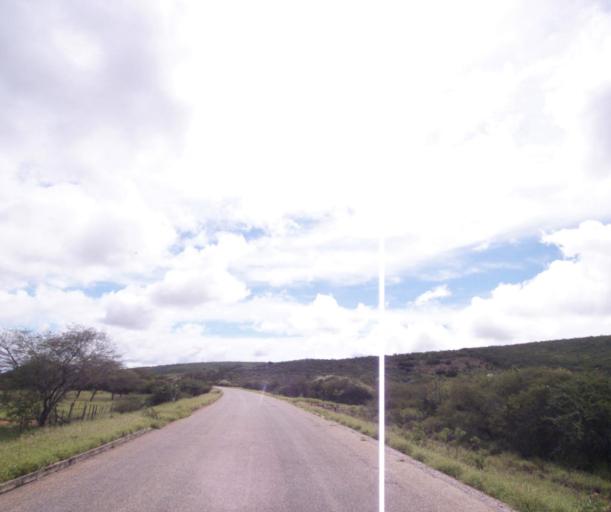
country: BR
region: Bahia
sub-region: Brumado
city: Brumado
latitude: -14.1969
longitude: -41.5853
